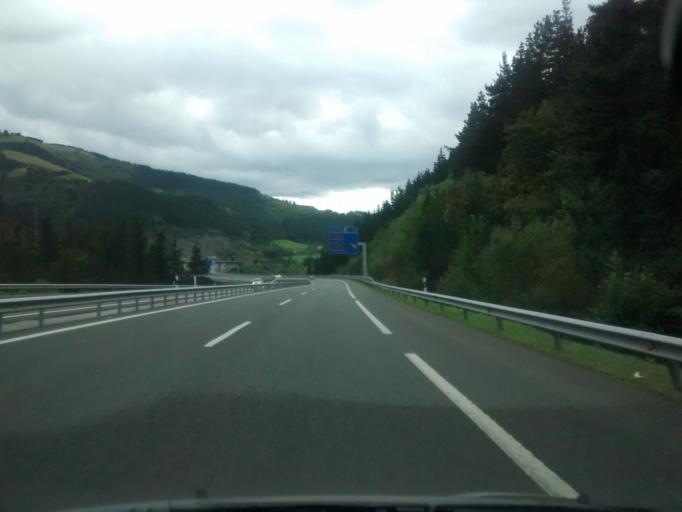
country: ES
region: Basque Country
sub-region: Provincia de Guipuzcoa
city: Bergara
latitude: 43.0962
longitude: -2.4340
